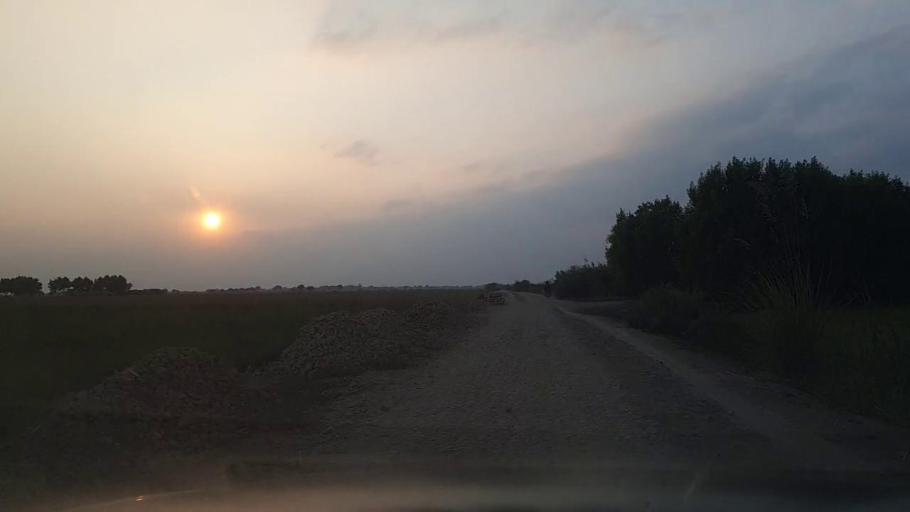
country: PK
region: Sindh
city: Jati
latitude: 24.5297
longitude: 68.4017
